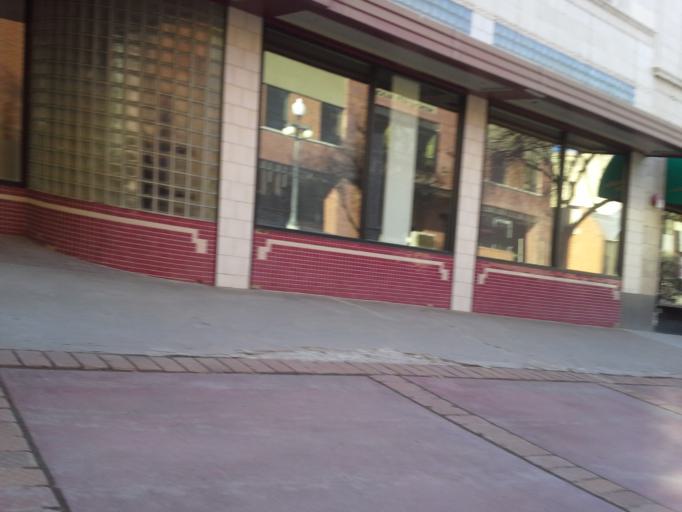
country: US
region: Montana
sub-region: Lewis and Clark County
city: Helena
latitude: 46.5880
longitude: -112.0390
